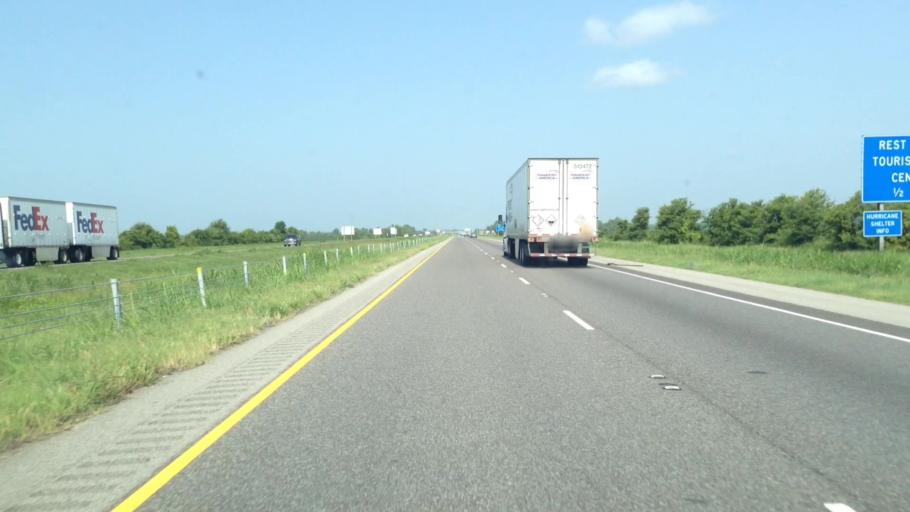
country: US
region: Mississippi
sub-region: Warren County
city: Vicksburg
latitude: 32.3226
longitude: -90.9759
